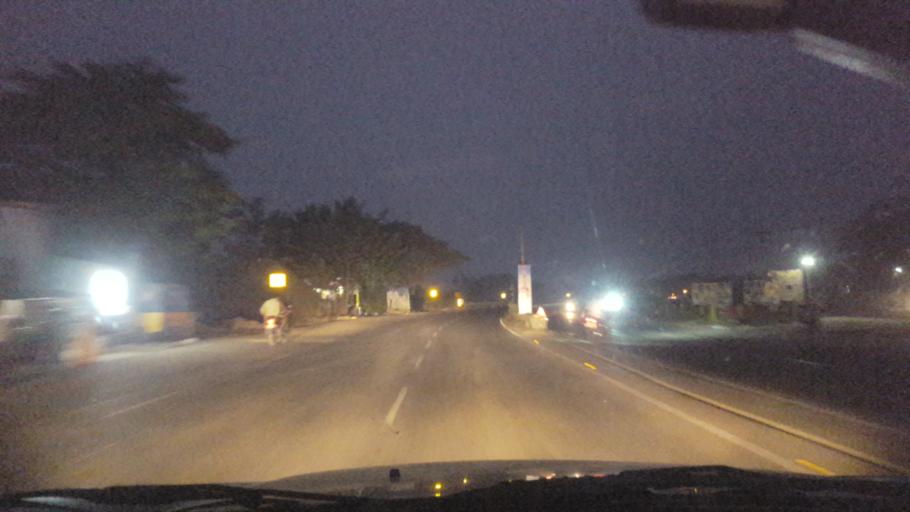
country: IN
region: Andhra Pradesh
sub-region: East Godavari
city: Peddapuram
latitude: 17.1372
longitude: 81.9593
